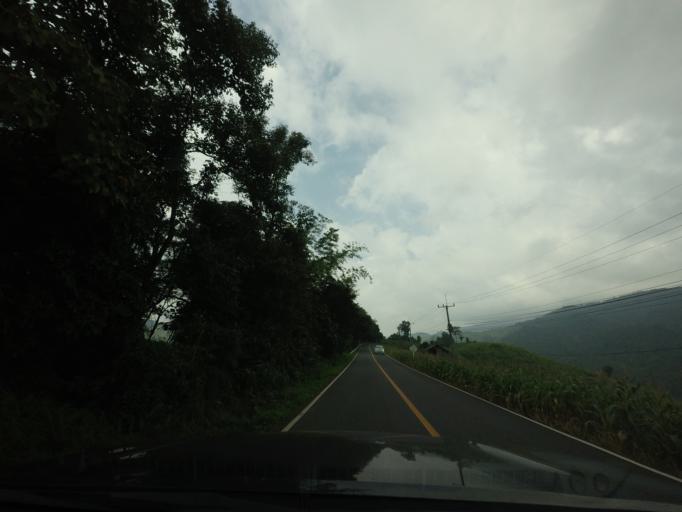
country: TH
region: Nan
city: Bo Kluea
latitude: 19.1974
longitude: 101.0538
